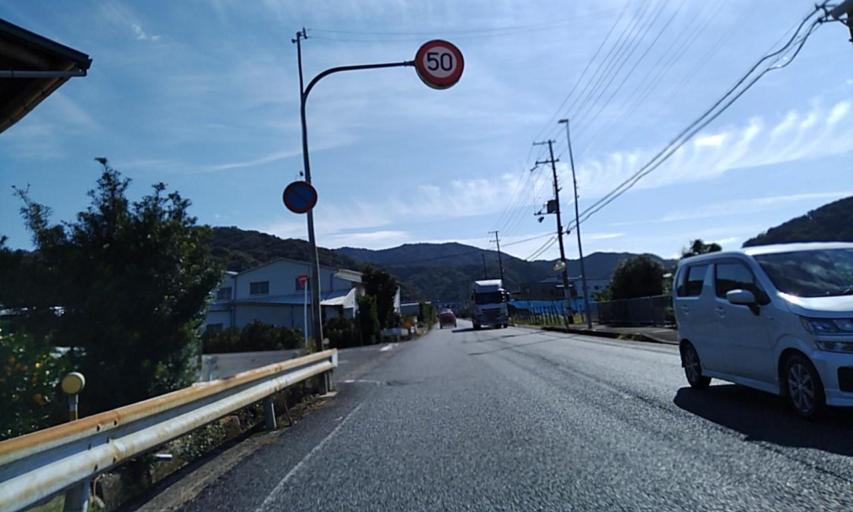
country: JP
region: Wakayama
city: Kainan
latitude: 34.0177
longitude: 135.1839
